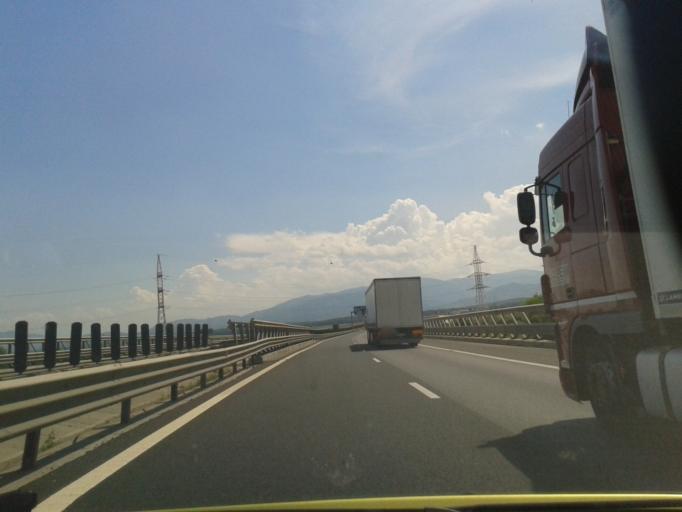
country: RO
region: Sibiu
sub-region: Comuna Selimbar
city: Selimbar
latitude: 45.7595
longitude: 24.2070
